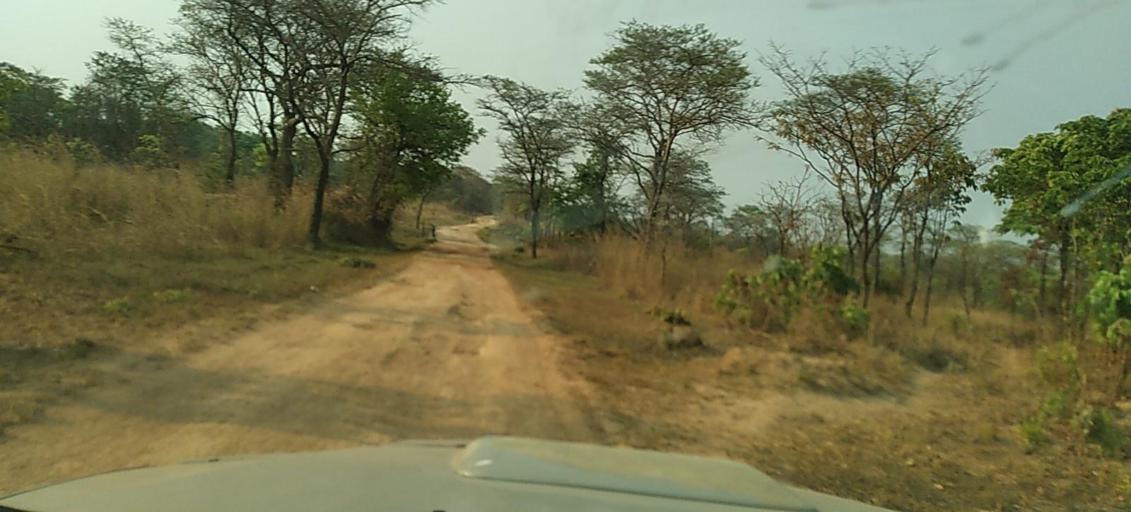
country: ZM
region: North-Western
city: Kasempa
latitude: -13.2833
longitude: 26.5550
